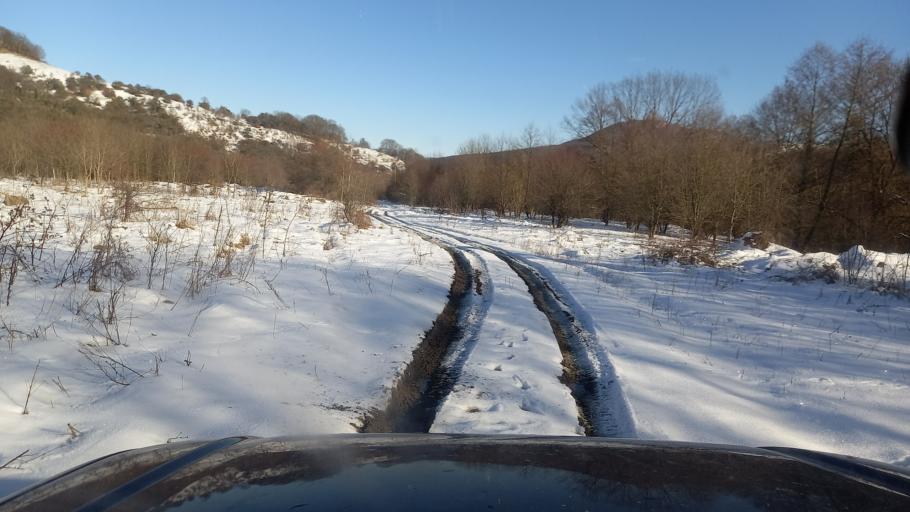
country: RU
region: Adygeya
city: Kamennomostskiy
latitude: 44.2050
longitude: 40.1419
